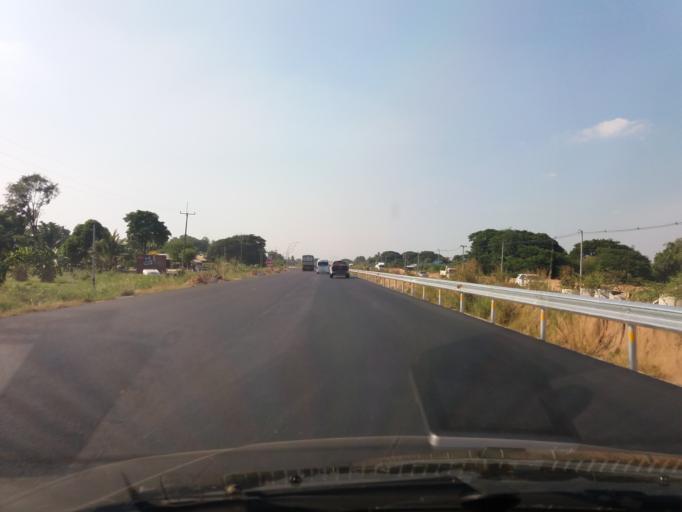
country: TH
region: Nakhon Sawan
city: Krok Phra
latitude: 15.6273
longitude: 100.1081
